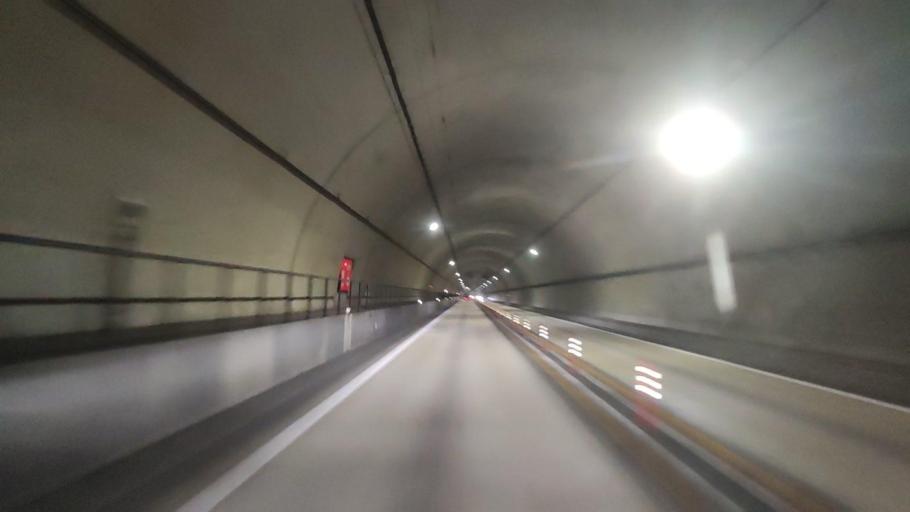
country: JP
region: Wakayama
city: Tanabe
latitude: 33.5677
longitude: 135.4902
